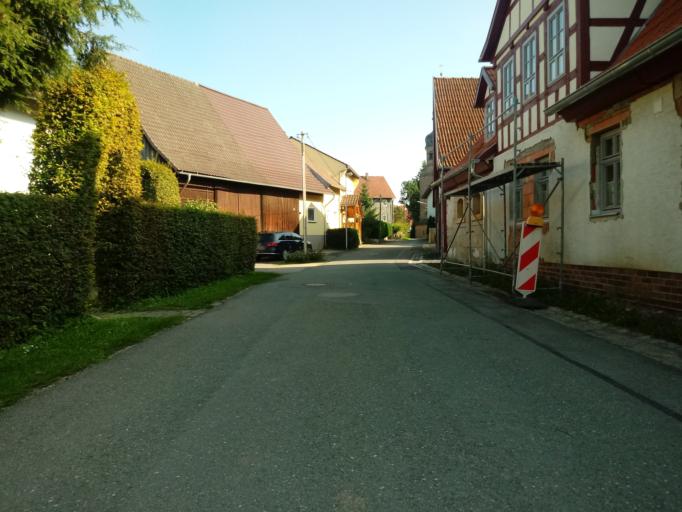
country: DE
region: Bavaria
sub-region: Upper Franconia
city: Grossheirath
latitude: 50.1787
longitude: 10.9484
